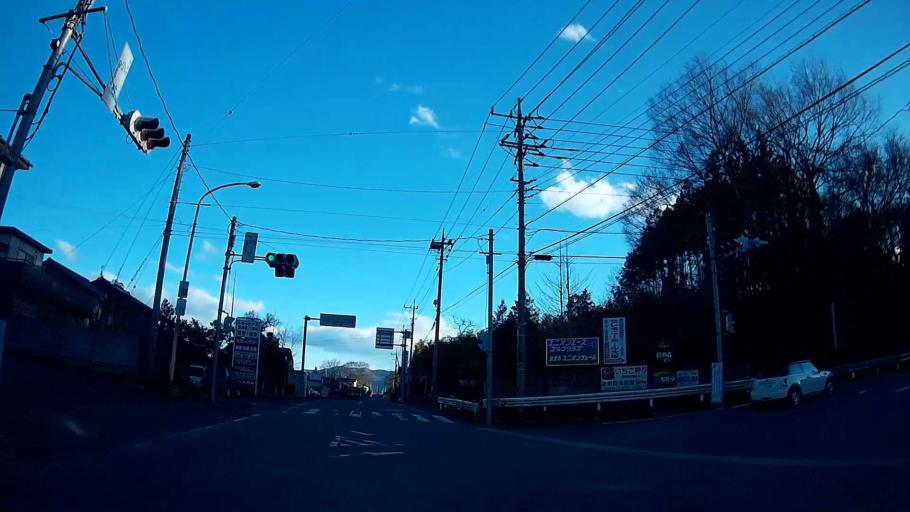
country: JP
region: Saitama
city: Chichibu
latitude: 36.0643
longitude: 139.0868
